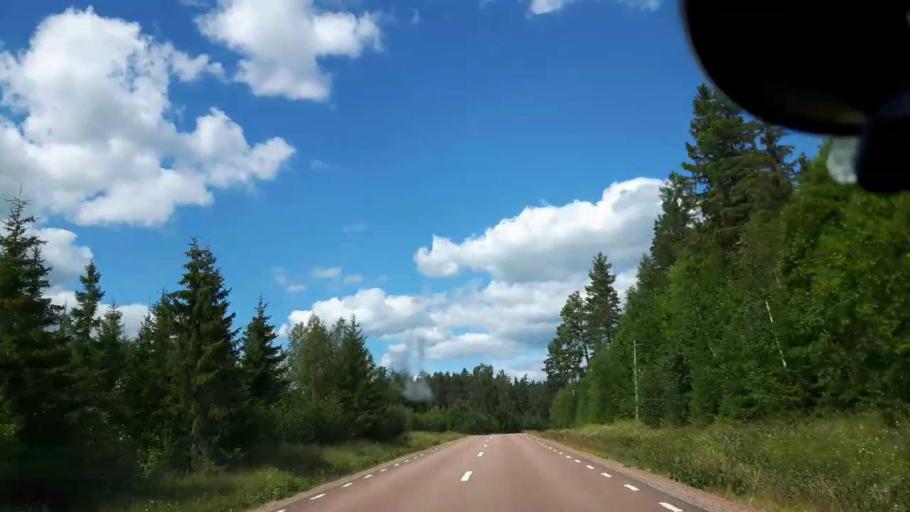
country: SE
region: Jaemtland
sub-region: Ragunda Kommun
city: Hammarstrand
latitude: 63.0322
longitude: 16.5203
